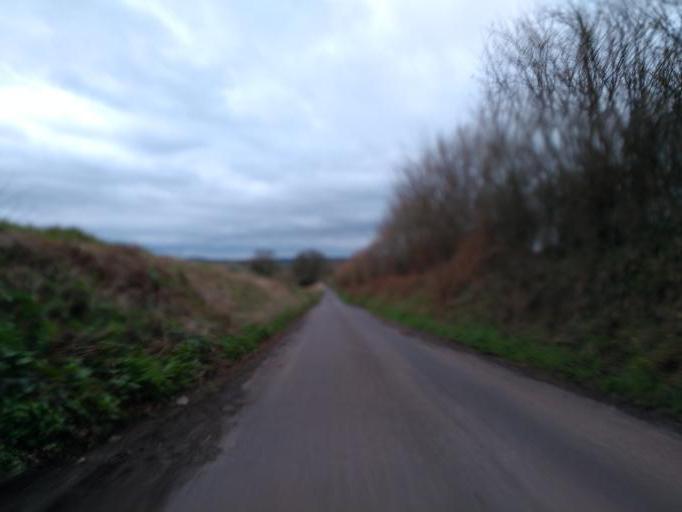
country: GB
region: England
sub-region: Devon
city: Bradninch
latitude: 50.8081
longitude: -3.4869
